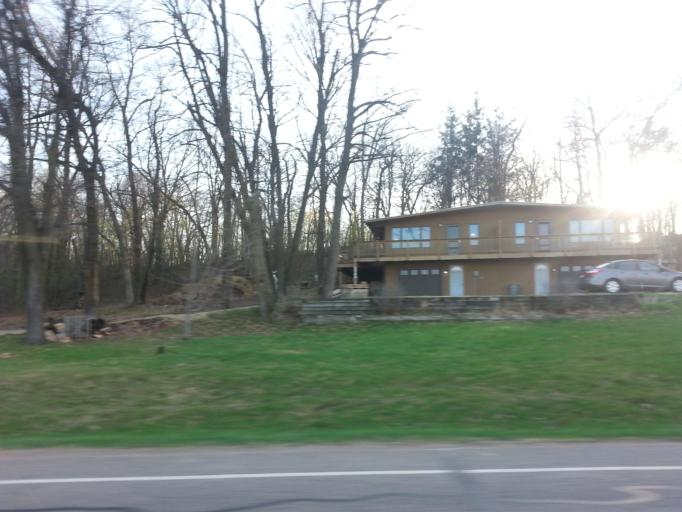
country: US
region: Wisconsin
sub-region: Pierce County
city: River Falls
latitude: 44.9081
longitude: -92.6791
